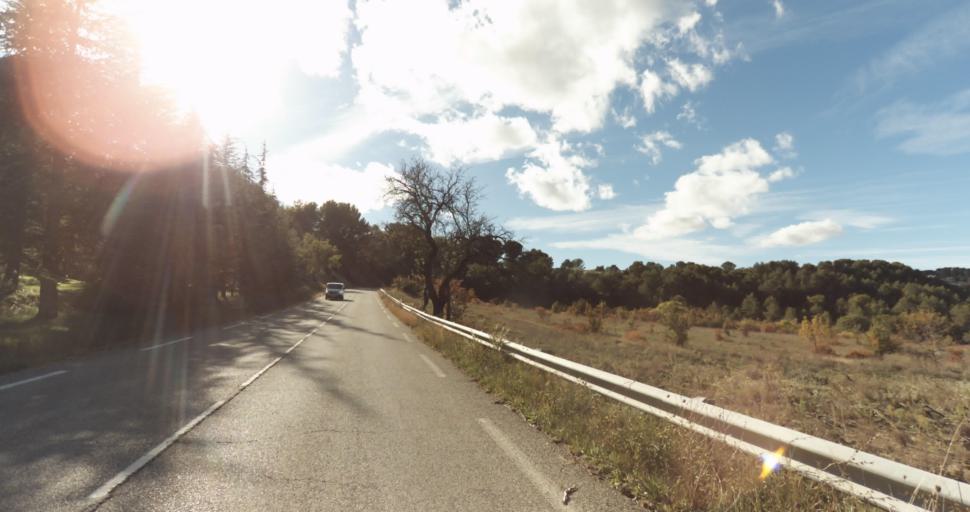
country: FR
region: Provence-Alpes-Cote d'Azur
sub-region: Departement des Bouches-du-Rhone
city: Venelles
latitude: 43.6015
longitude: 5.4936
